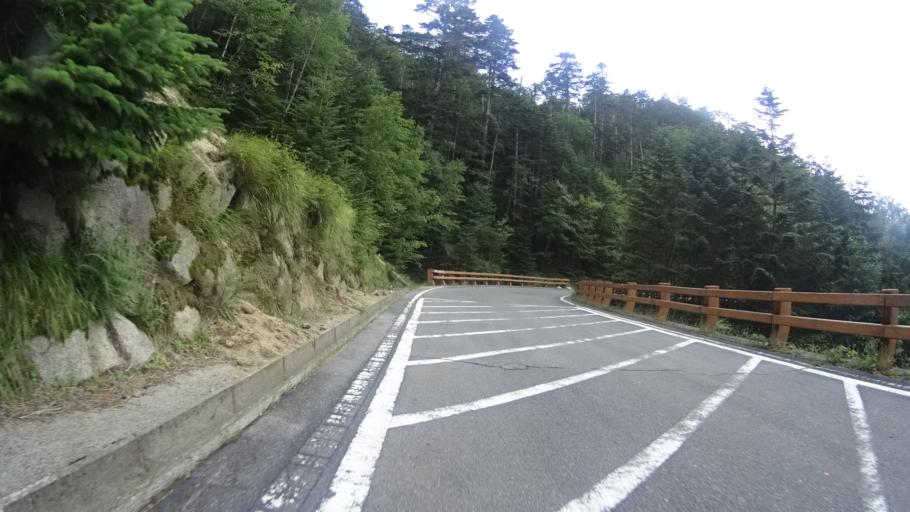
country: JP
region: Yamanashi
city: Enzan
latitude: 35.8662
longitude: 138.6625
